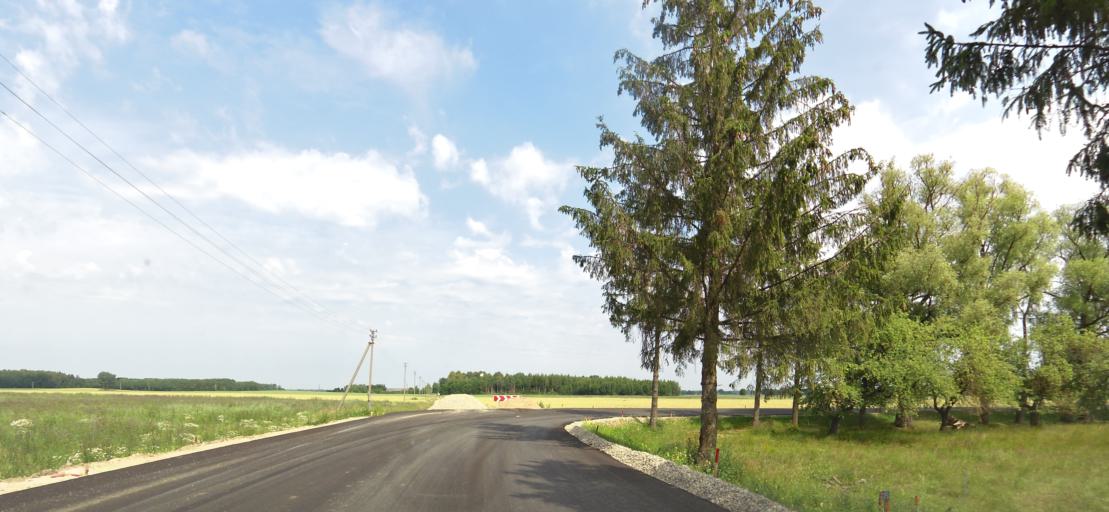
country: LT
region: Panevezys
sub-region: Birzai
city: Birzai
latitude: 56.2968
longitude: 24.6064
